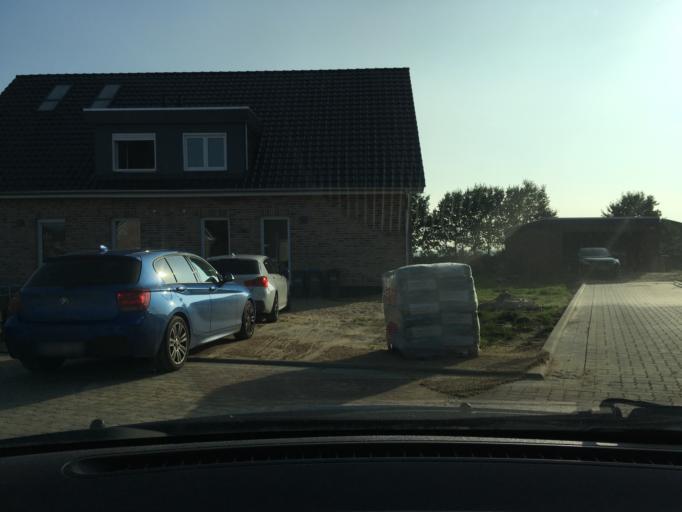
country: DE
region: Lower Saxony
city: Artlenburg
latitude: 53.3706
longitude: 10.4942
